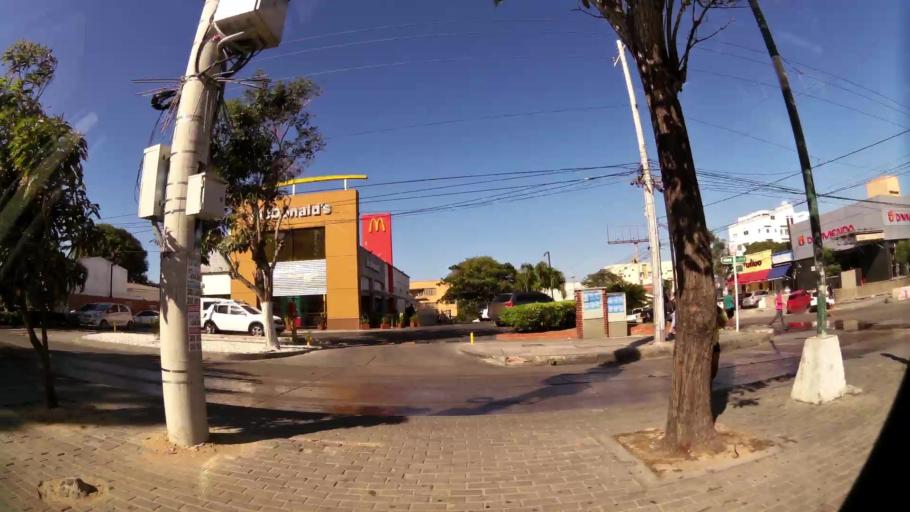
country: CO
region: Atlantico
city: Barranquilla
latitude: 11.0047
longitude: -74.8271
